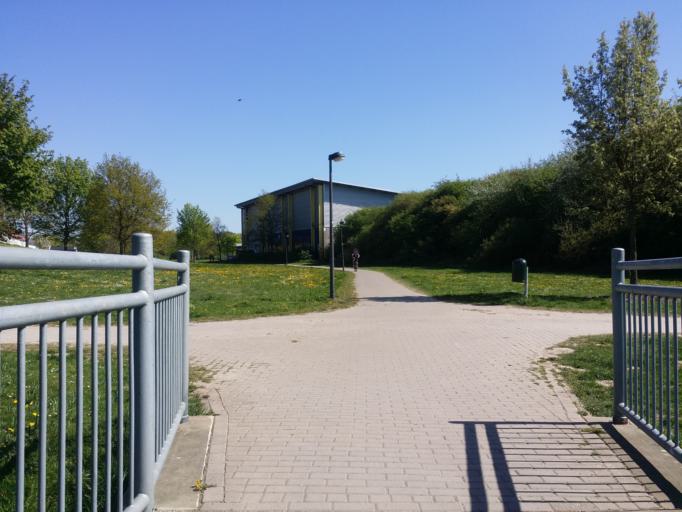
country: DE
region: Bremen
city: Bremen
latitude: 53.0274
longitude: 8.8321
